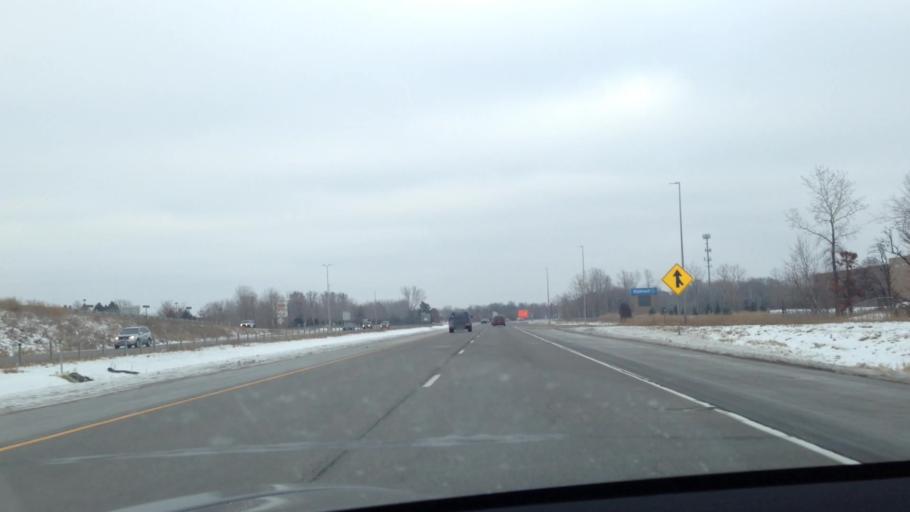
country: US
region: Minnesota
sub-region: Anoka County
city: Circle Pines
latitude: 45.1600
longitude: -93.1623
